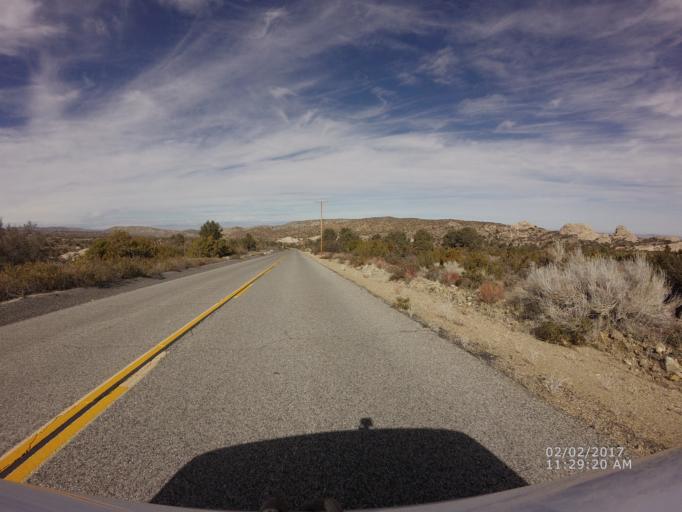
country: US
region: California
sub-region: Los Angeles County
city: Littlerock
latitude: 34.4249
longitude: -117.8688
